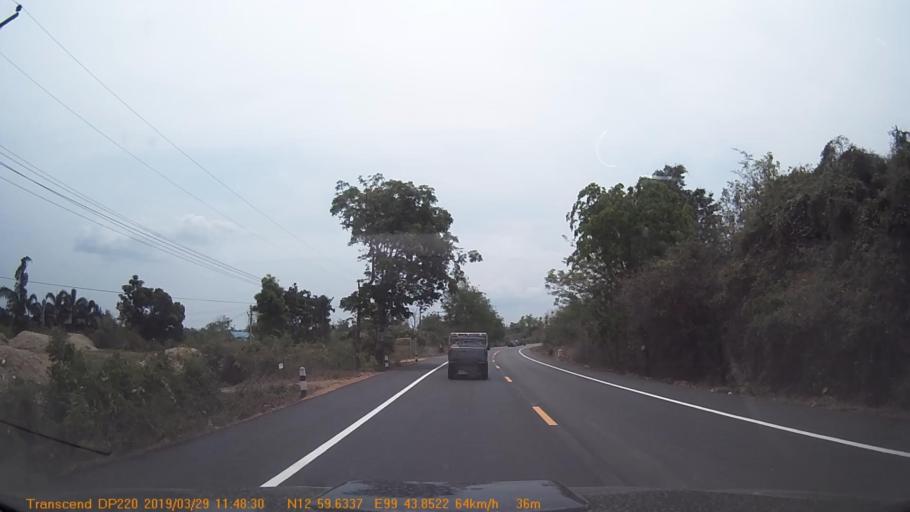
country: TH
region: Phetchaburi
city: Kaeng Krachan
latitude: 12.9936
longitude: 99.7311
